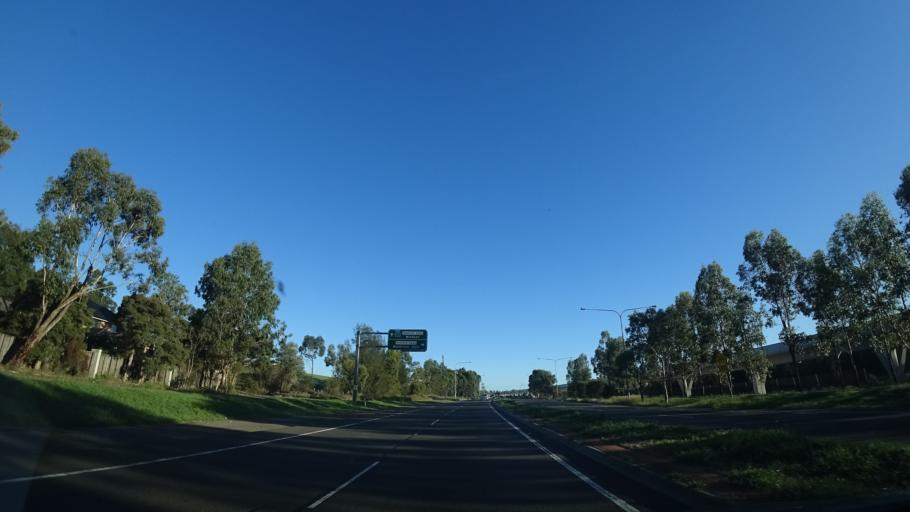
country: AU
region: New South Wales
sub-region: Blacktown
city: Stanhope Gardens
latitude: -33.7072
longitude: 150.9310
